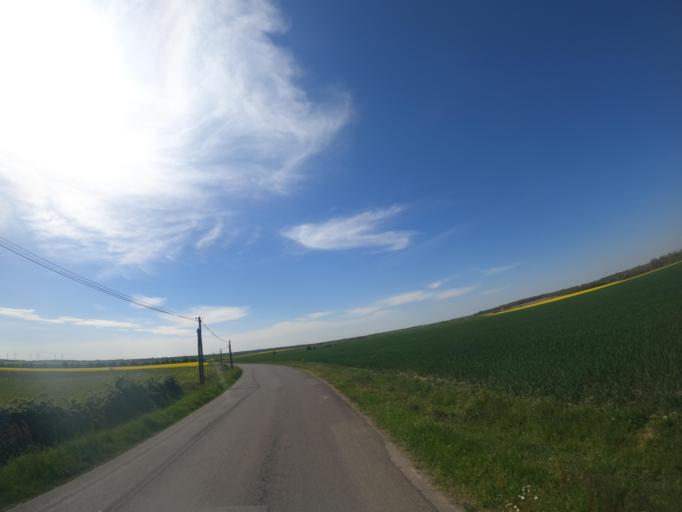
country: FR
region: Poitou-Charentes
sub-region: Departement des Deux-Sevres
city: Airvault
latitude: 46.8885
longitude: -0.1579
